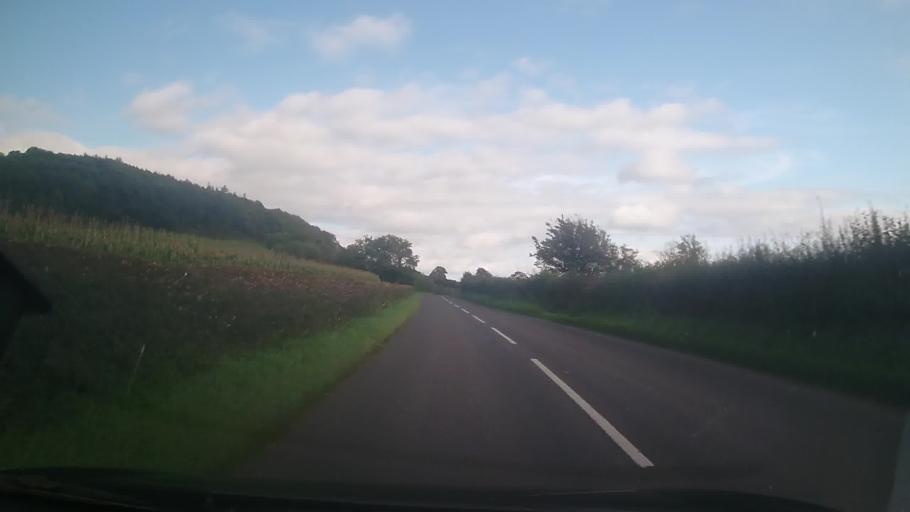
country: GB
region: England
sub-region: Shropshire
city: Bishop's Castle
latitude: 52.4684
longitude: -2.9769
